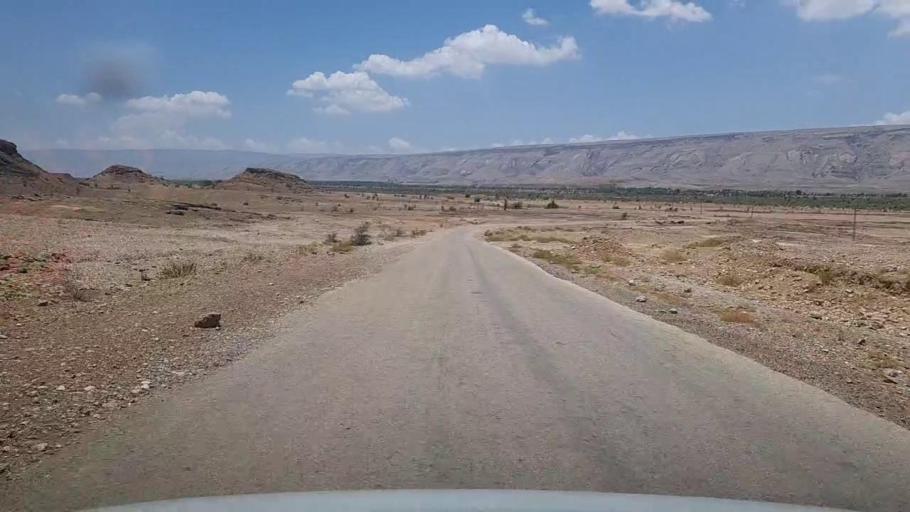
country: PK
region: Sindh
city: Bhan
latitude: 26.3123
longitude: 67.5418
